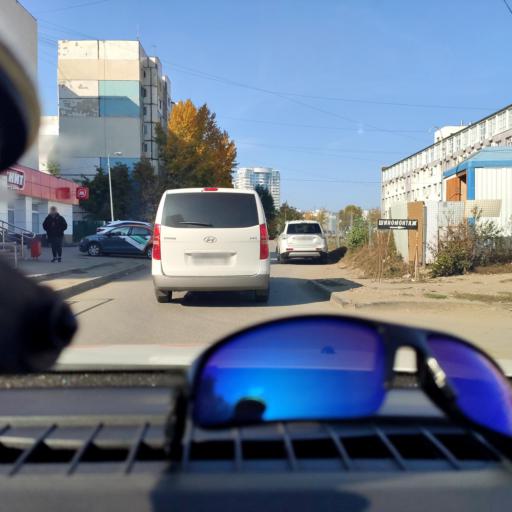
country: RU
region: Samara
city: Samara
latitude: 53.2485
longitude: 50.2145
